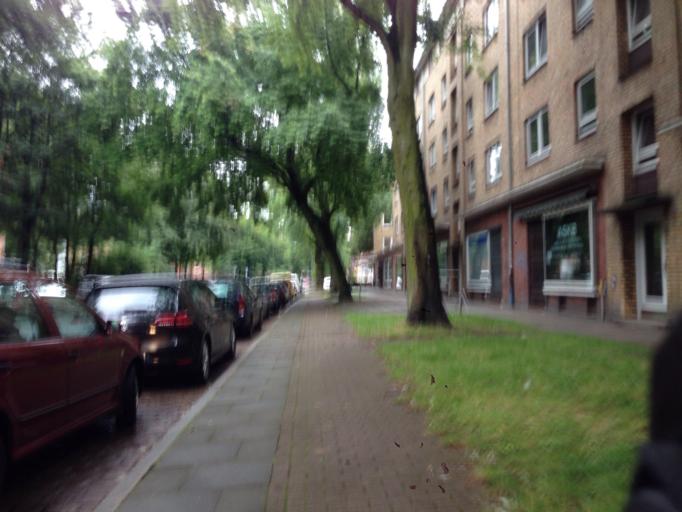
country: DE
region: Hamburg
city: Marienthal
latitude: 53.5516
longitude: 10.0873
